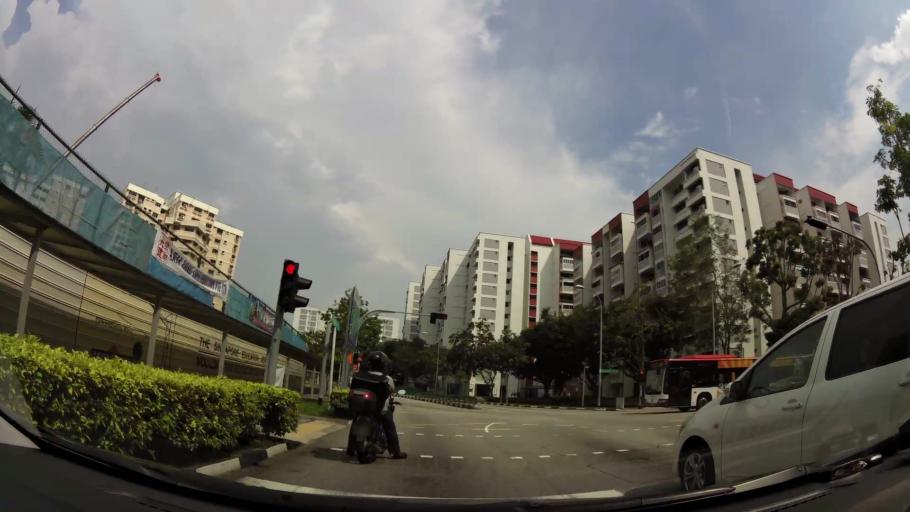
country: SG
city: Singapore
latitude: 1.3599
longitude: 103.9493
